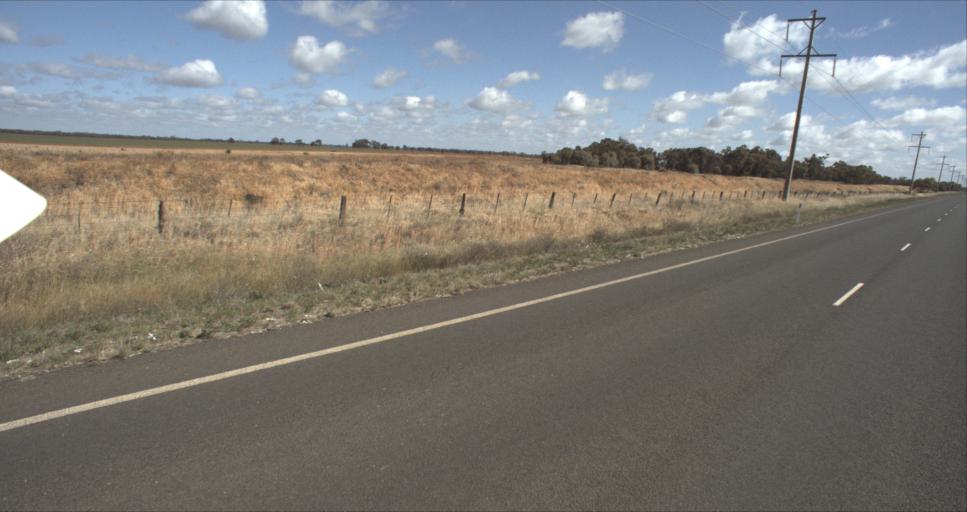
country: AU
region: New South Wales
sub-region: Murrumbidgee Shire
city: Darlington Point
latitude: -34.5335
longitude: 146.1735
